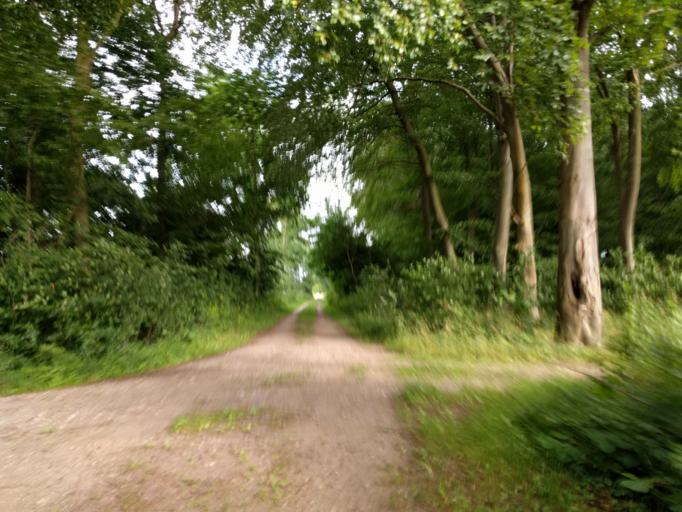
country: DK
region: South Denmark
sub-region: Kerteminde Kommune
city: Munkebo
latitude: 55.4256
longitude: 10.5531
